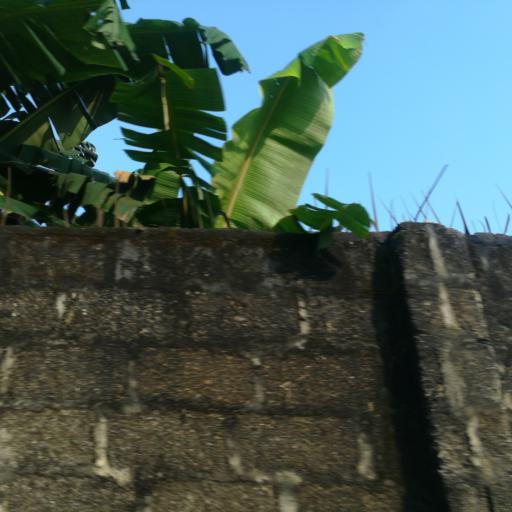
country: NG
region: Rivers
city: Port Harcourt
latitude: 4.8600
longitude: 6.9650
